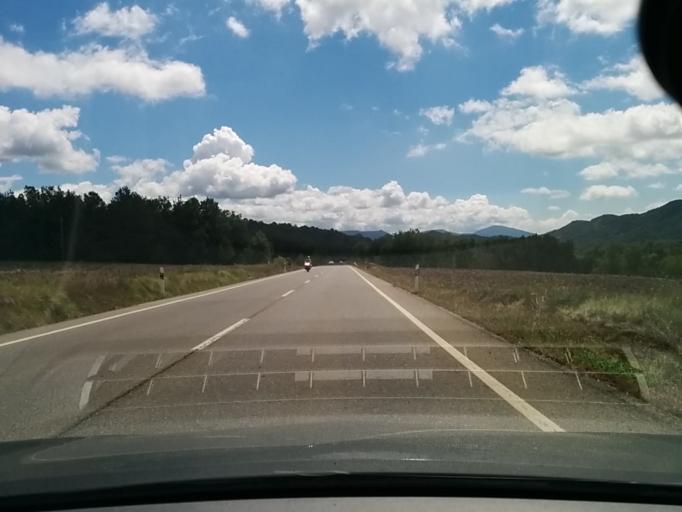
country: ES
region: Aragon
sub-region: Provincia de Huesca
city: Ainsa
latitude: 42.4280
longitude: 0.1171
